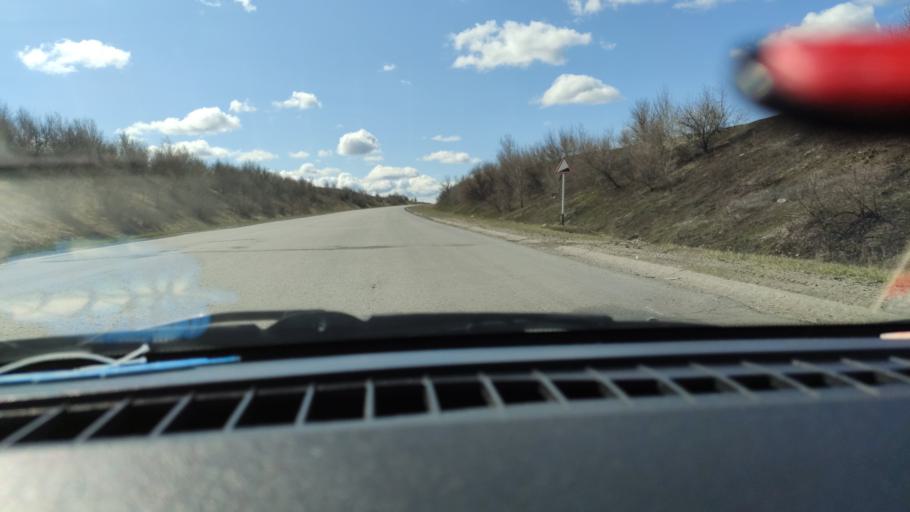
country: RU
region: Samara
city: Varlamovo
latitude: 53.0637
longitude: 48.3530
